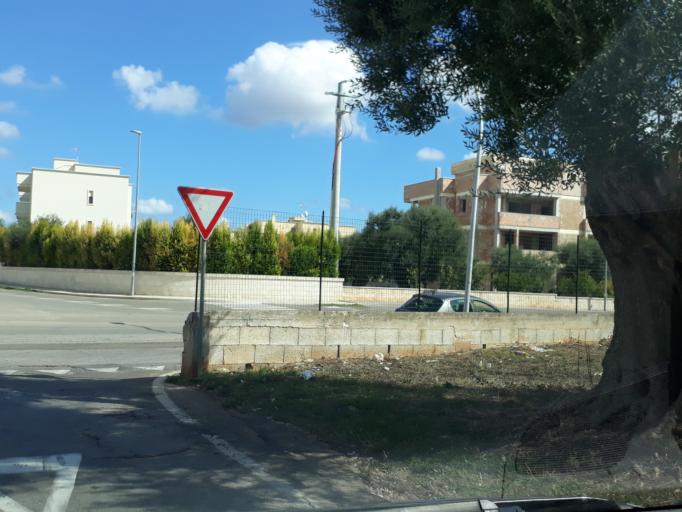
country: IT
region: Apulia
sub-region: Provincia di Brindisi
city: Fasano
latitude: 40.8296
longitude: 17.3660
